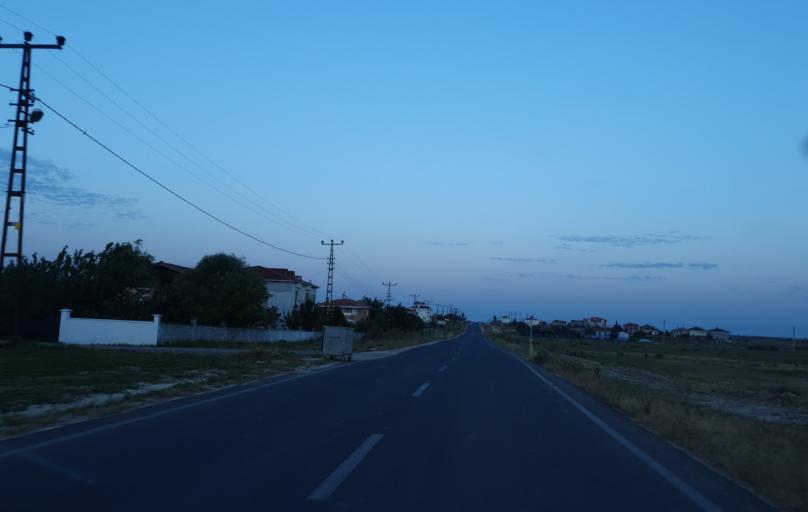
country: TR
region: Tekirdag
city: Velimese
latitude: 41.3458
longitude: 27.8933
